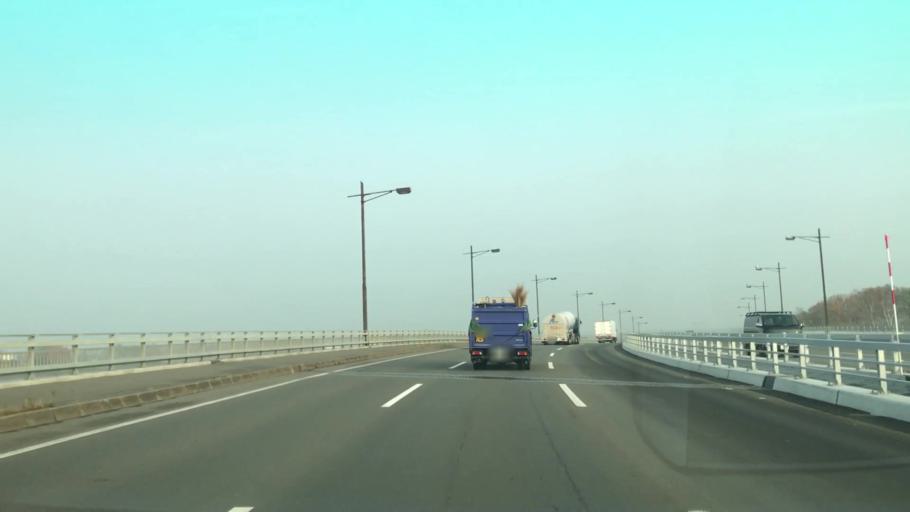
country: JP
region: Hokkaido
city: Ishikari
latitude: 43.1669
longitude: 141.3488
